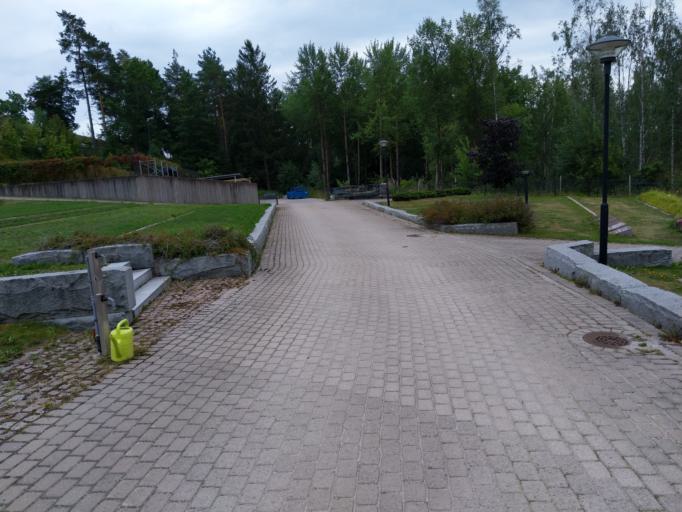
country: FI
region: Varsinais-Suomi
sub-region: Salo
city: Halikko
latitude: 60.3998
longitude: 23.0701
